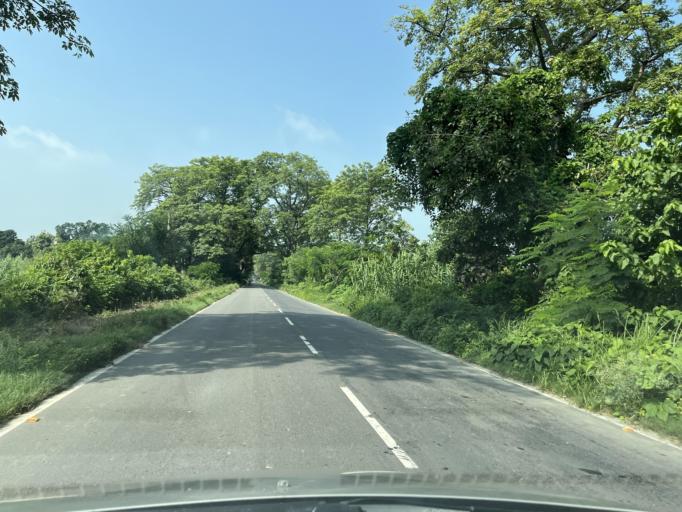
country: IN
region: Uttarakhand
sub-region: Udham Singh Nagar
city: Bazpur
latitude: 29.1915
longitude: 79.1921
